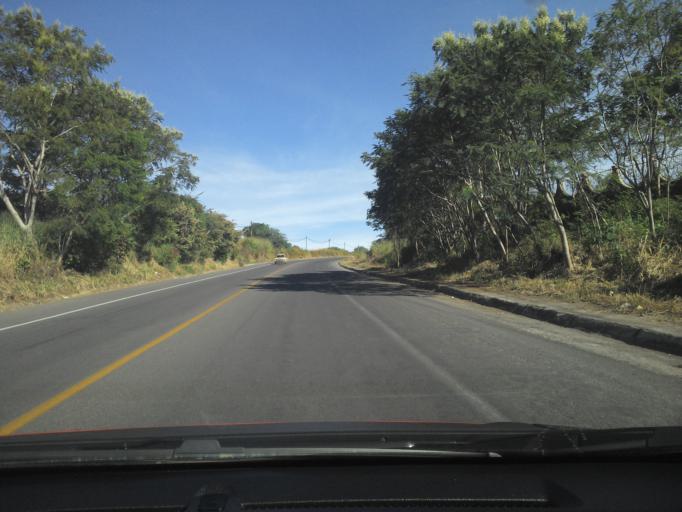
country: MX
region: Jalisco
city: Teuchitlan
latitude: 20.6803
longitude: -103.8431
